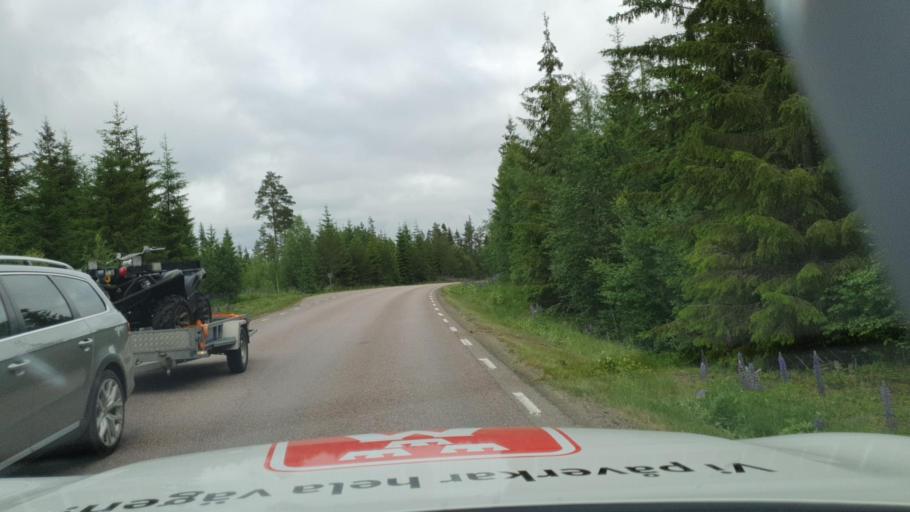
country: SE
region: Vaermland
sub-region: Arvika Kommun
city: Arvika
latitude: 59.9472
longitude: 12.6924
